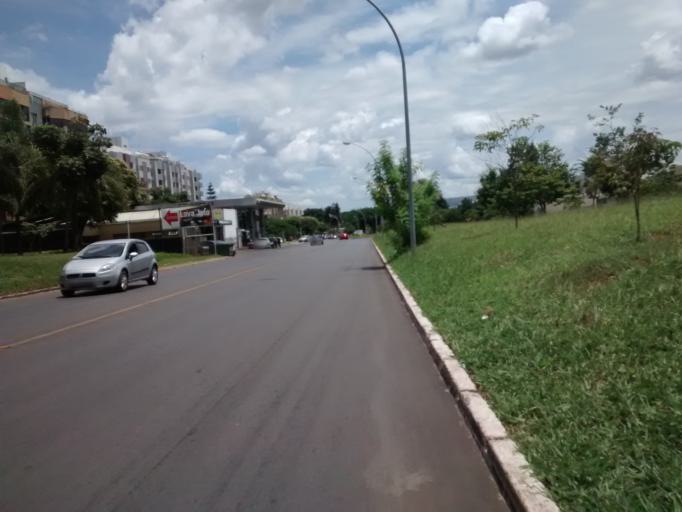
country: BR
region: Federal District
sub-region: Brasilia
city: Brasilia
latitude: -15.7614
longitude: -47.8880
